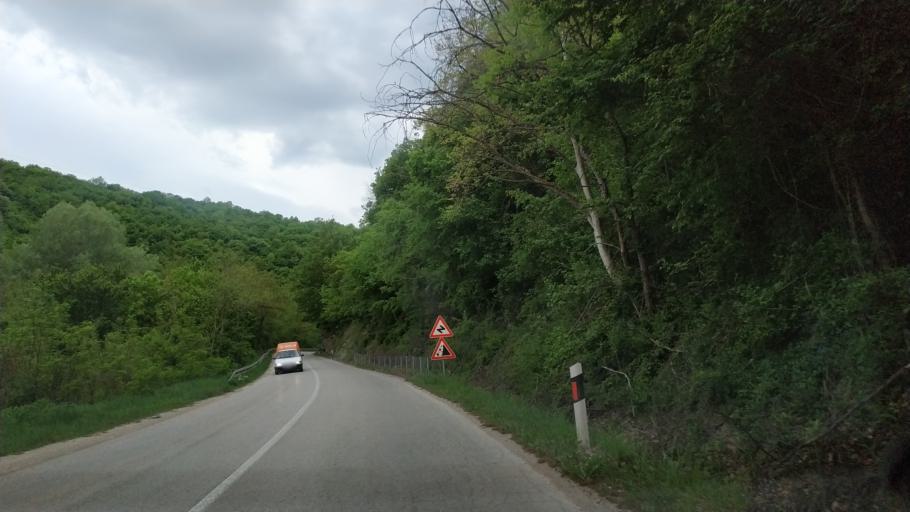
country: RS
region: Central Serbia
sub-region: Nisavski Okrug
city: Aleksinac
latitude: 43.6229
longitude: 21.6984
